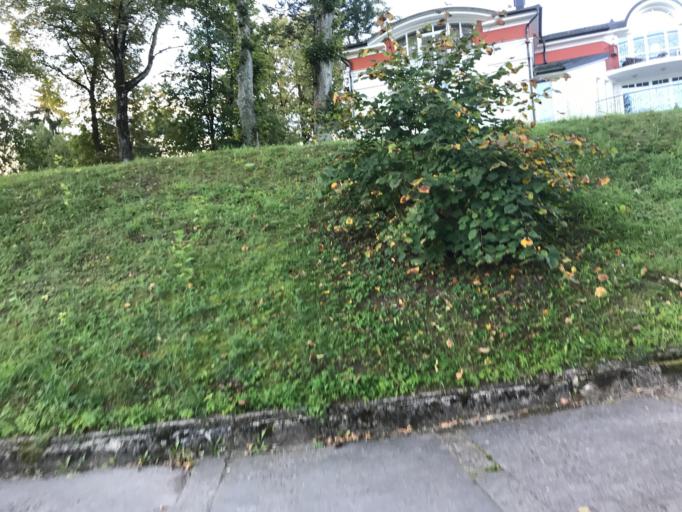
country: LT
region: Alytaus apskritis
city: Druskininkai
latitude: 54.0186
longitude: 23.9834
